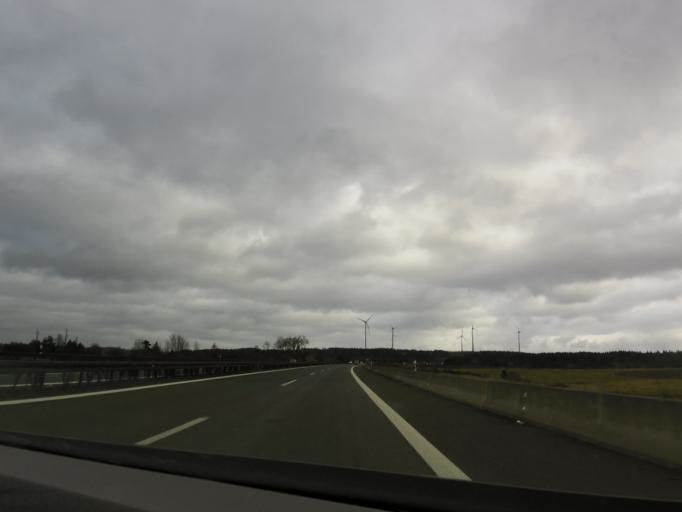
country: DE
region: Bavaria
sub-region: Upper Franconia
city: Gattendorf
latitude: 50.3412
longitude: 12.0060
